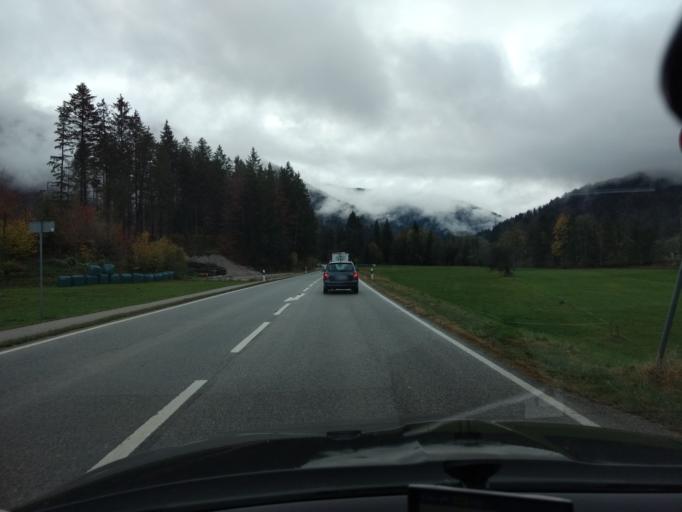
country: DE
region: Bavaria
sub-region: Upper Bavaria
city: Lenggries
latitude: 47.6333
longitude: 11.5944
